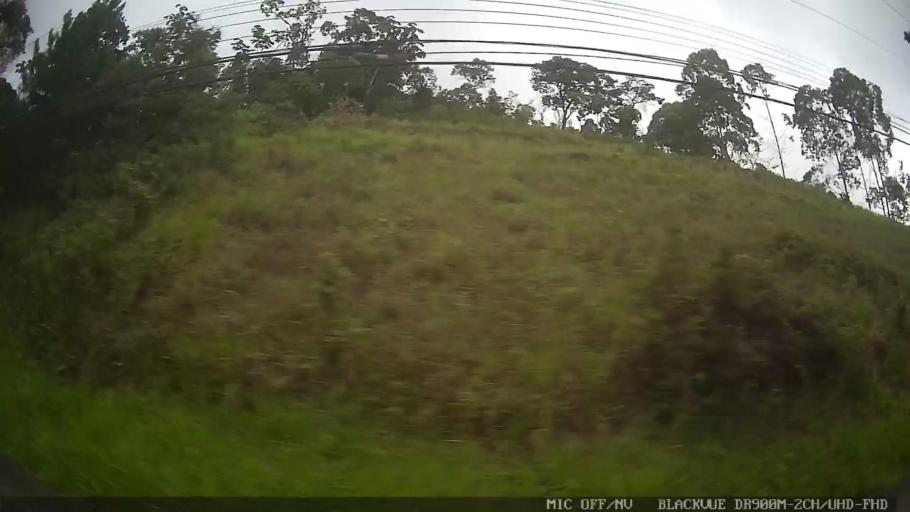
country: BR
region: Sao Paulo
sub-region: Mogi das Cruzes
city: Mogi das Cruzes
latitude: -23.4984
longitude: -46.2237
